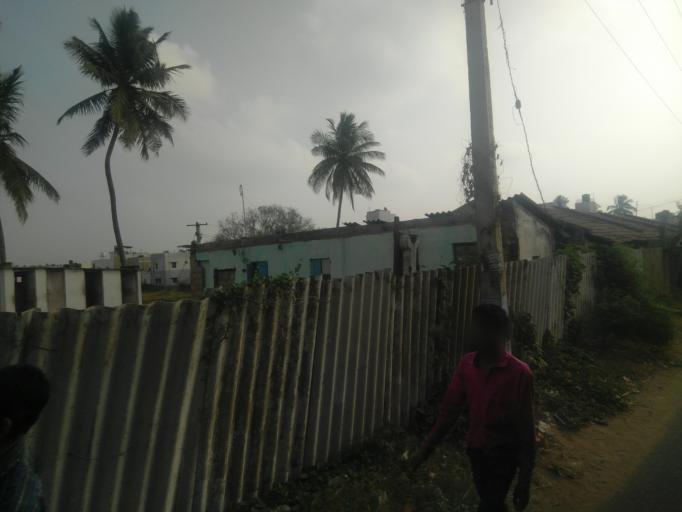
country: IN
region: Tamil Nadu
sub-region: Coimbatore
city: Coimbatore
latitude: 11.0650
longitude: 76.9121
